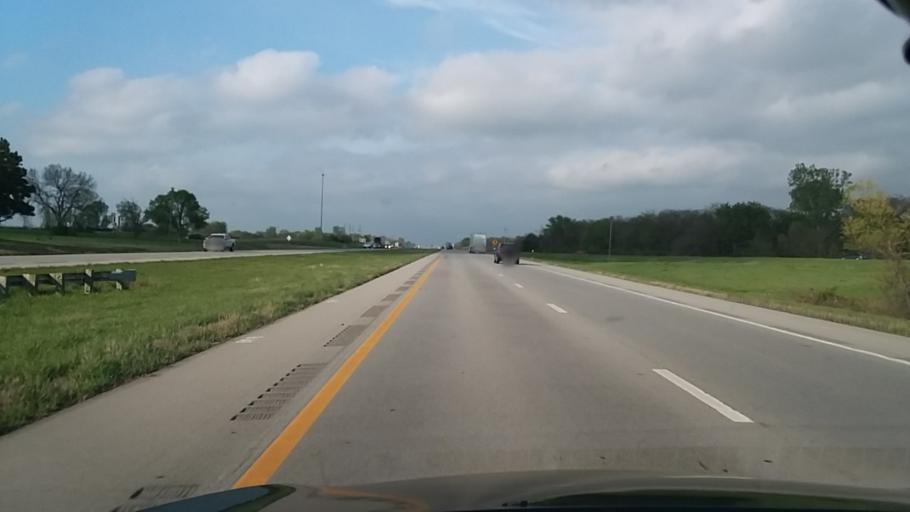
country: US
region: Kansas
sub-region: Johnson County
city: Gardner
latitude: 38.7817
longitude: -94.9271
